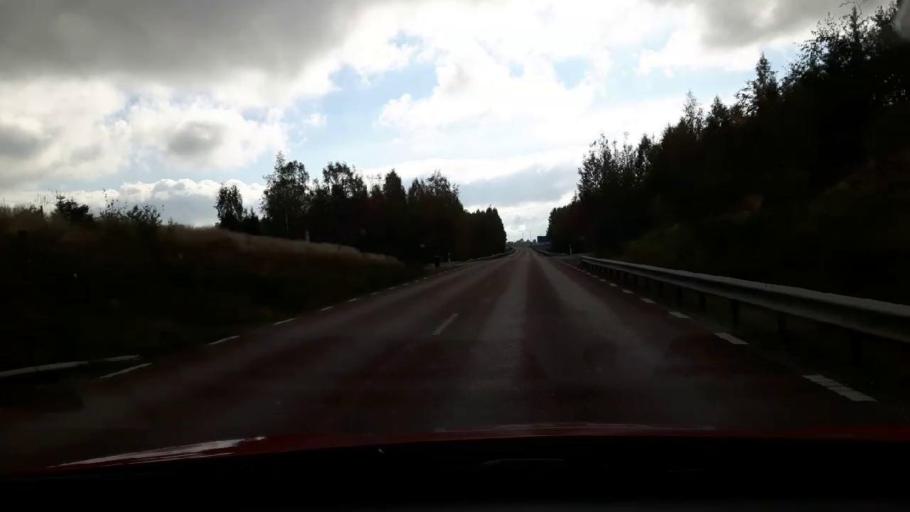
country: SE
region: Gaevleborg
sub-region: Bollnas Kommun
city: Arbra
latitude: 61.5480
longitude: 16.3516
